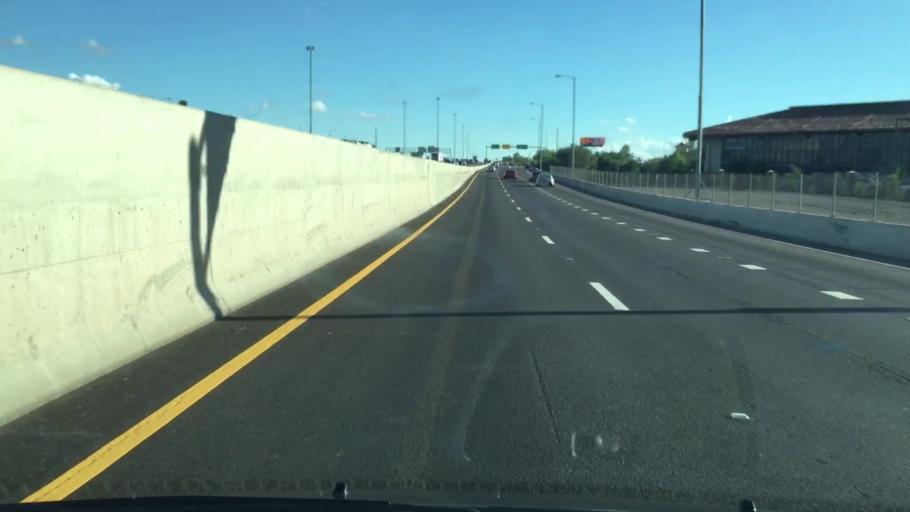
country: US
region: Arizona
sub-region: Maricopa County
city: Guadalupe
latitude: 33.3844
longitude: -111.9685
